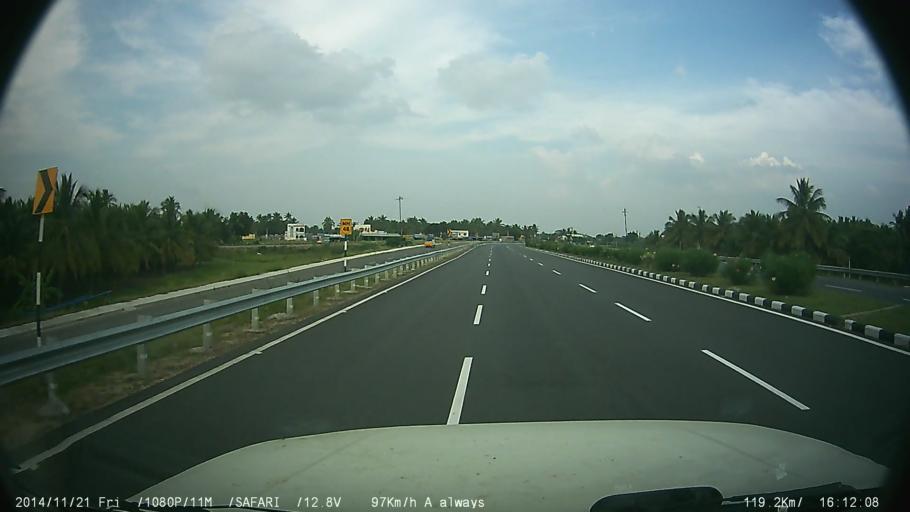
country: IN
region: Tamil Nadu
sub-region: Vellore
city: Jolarpettai
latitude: 12.5938
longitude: 78.5219
